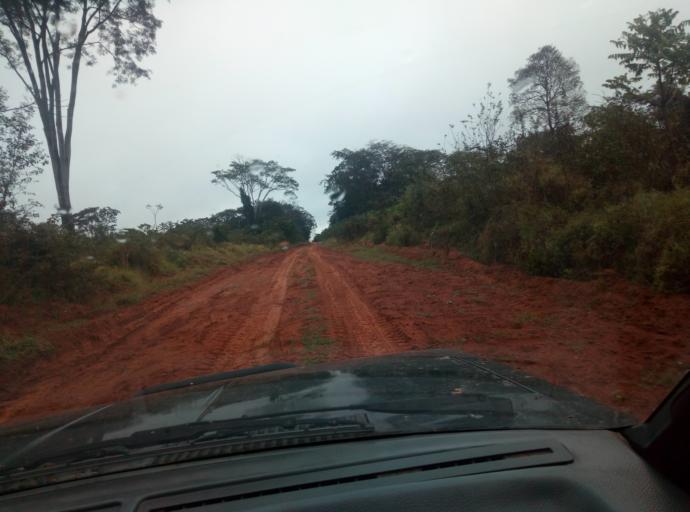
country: PY
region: Caaguazu
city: Carayao
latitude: -25.1921
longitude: -56.3392
